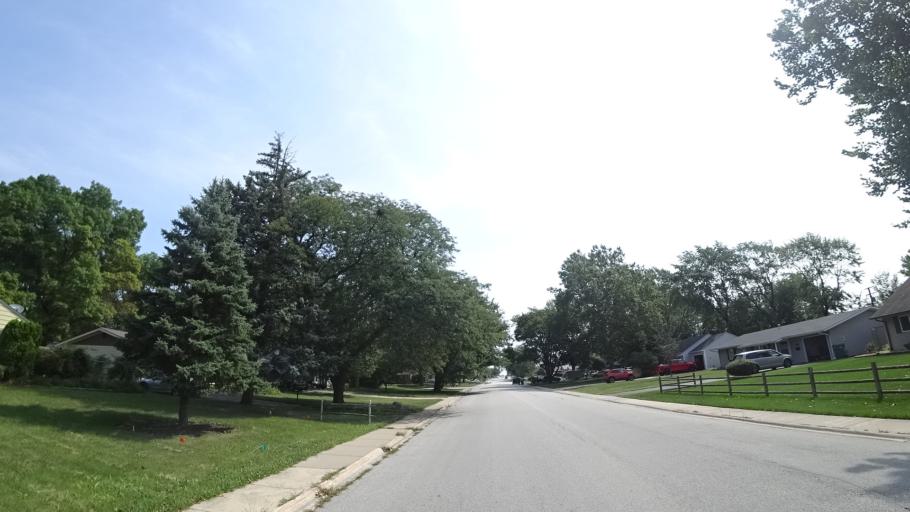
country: US
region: Illinois
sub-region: Cook County
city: Orland Park
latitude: 41.6157
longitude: -87.8666
